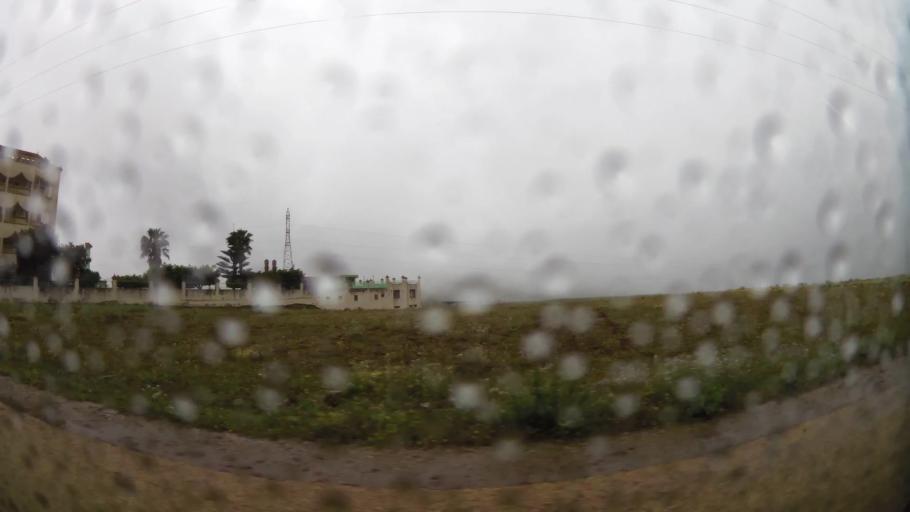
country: MA
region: Oriental
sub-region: Nador
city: Boudinar
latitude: 35.1278
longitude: -3.6471
